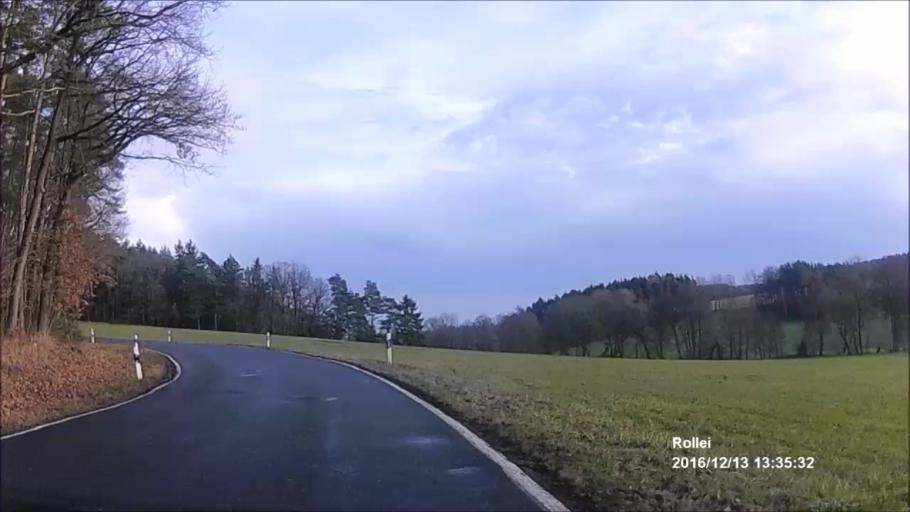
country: DE
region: Thuringia
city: Schwarza
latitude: 50.8500
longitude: 11.3056
